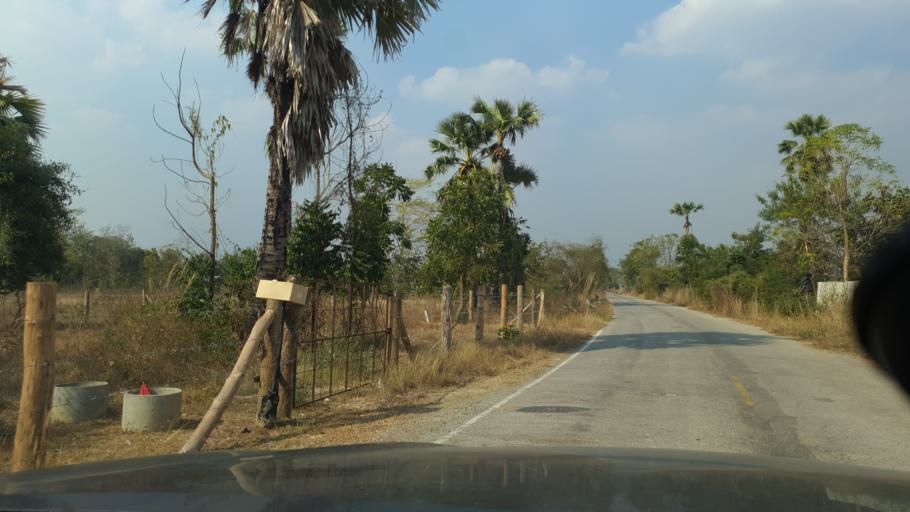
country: TH
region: Sukhothai
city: Ban Dan Lan Hoi
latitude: 17.0106
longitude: 99.5582
